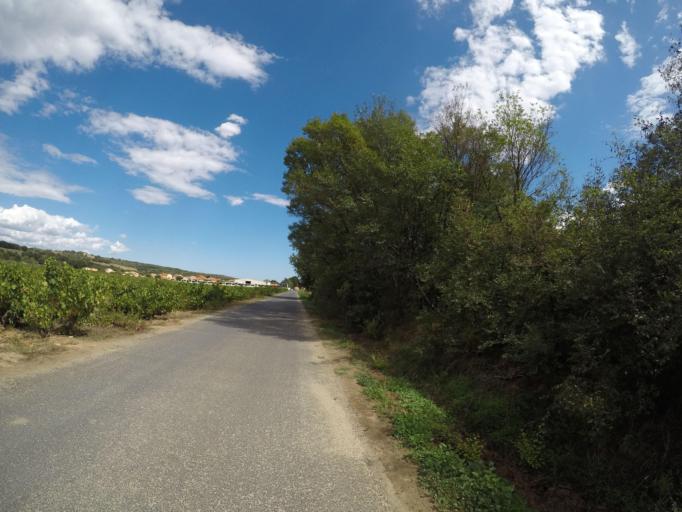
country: FR
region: Languedoc-Roussillon
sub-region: Departement des Pyrenees-Orientales
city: Sant Joan de Pladecorts
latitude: 42.5133
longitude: 2.7825
